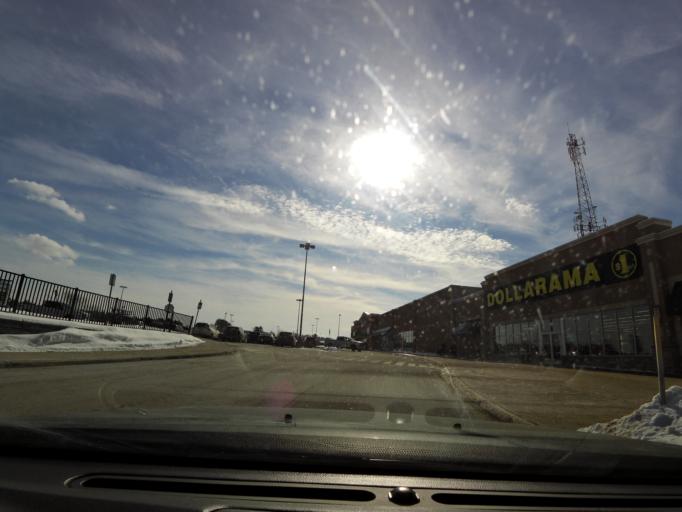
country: CA
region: Ontario
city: Gravenhurst
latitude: 44.9085
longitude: -79.3708
